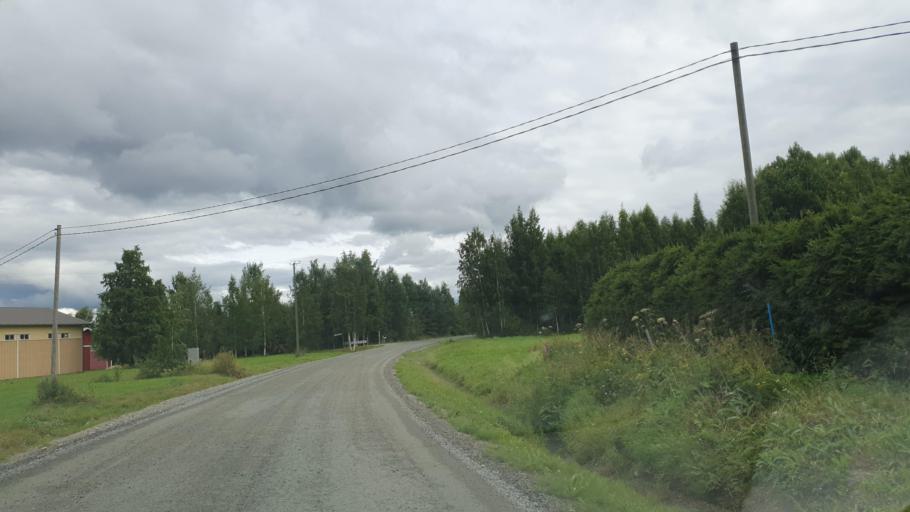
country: FI
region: Northern Savo
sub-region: Ylae-Savo
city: Iisalmi
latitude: 63.5368
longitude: 27.0810
